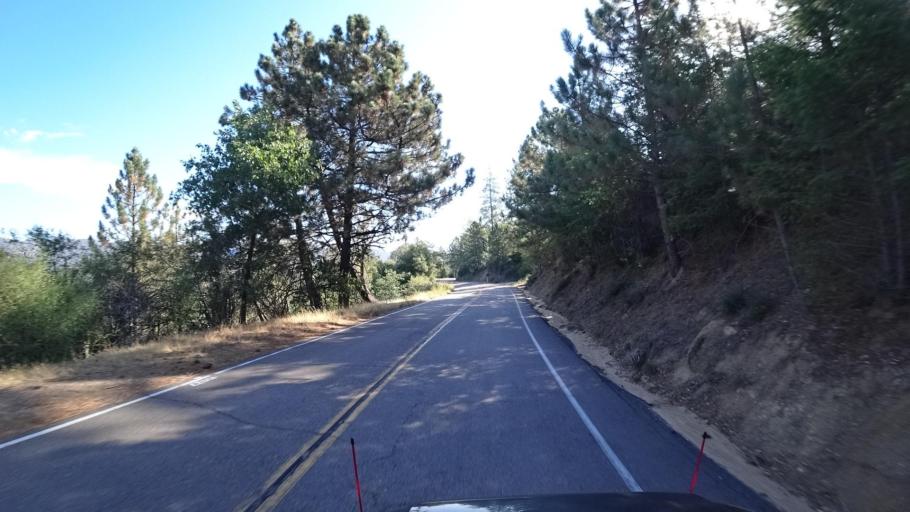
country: US
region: California
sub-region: Riverside County
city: Aguanga
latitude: 33.2873
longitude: -116.7997
